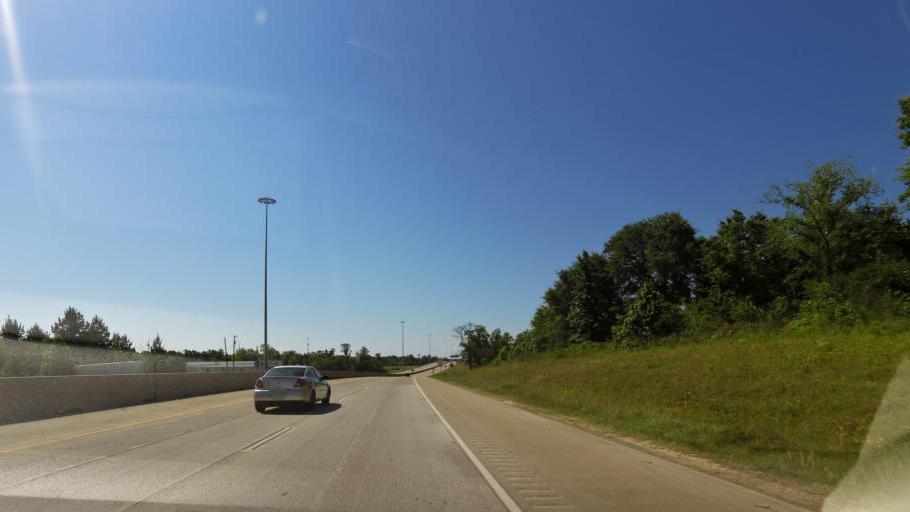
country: US
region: Texas
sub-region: Angelina County
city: Redland
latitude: 31.3821
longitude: -94.7128
